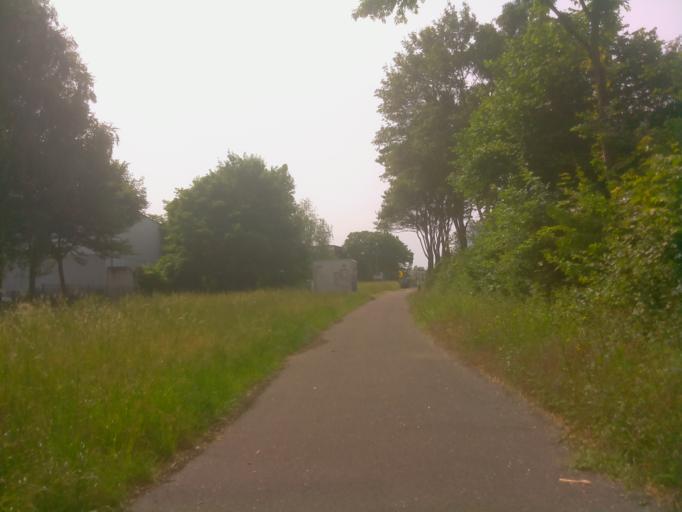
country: DE
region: Hesse
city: Viernheim
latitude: 49.5163
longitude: 8.5458
